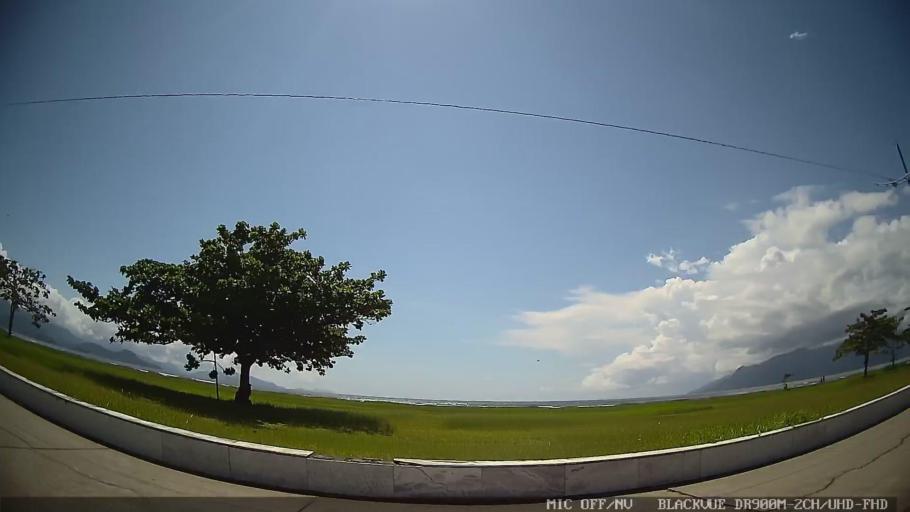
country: BR
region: Sao Paulo
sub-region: Caraguatatuba
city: Caraguatatuba
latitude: -23.6857
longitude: -45.4317
